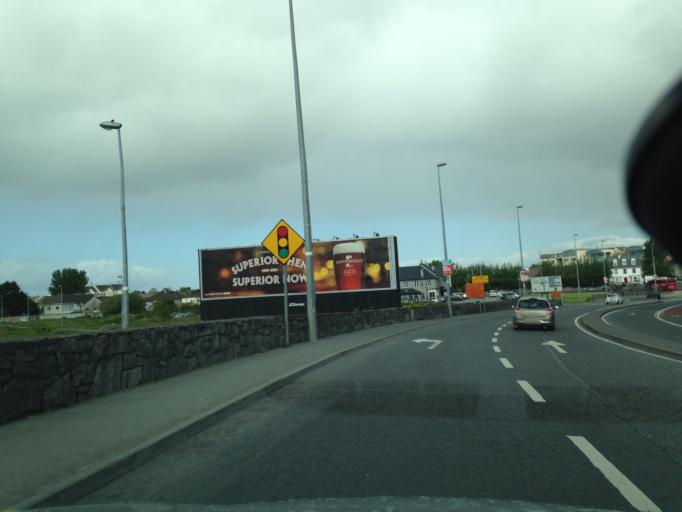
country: IE
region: Connaught
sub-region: County Galway
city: Gaillimh
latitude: 53.2809
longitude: -9.0312
